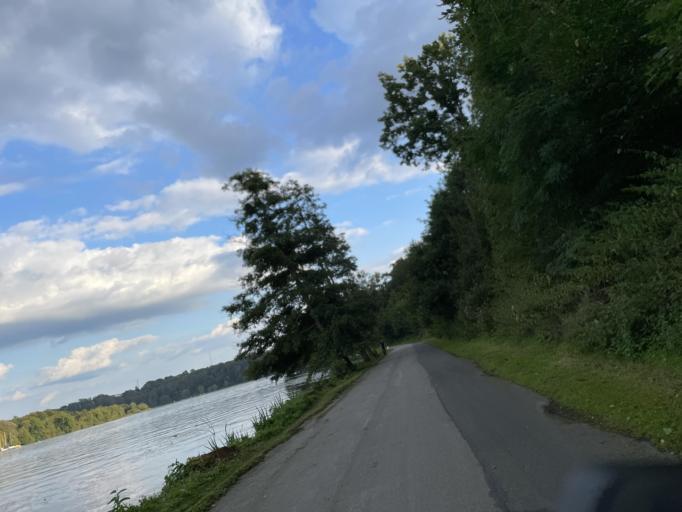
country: DE
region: North Rhine-Westphalia
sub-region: Regierungsbezirk Dusseldorf
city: Velbert
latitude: 51.3933
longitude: 7.0561
